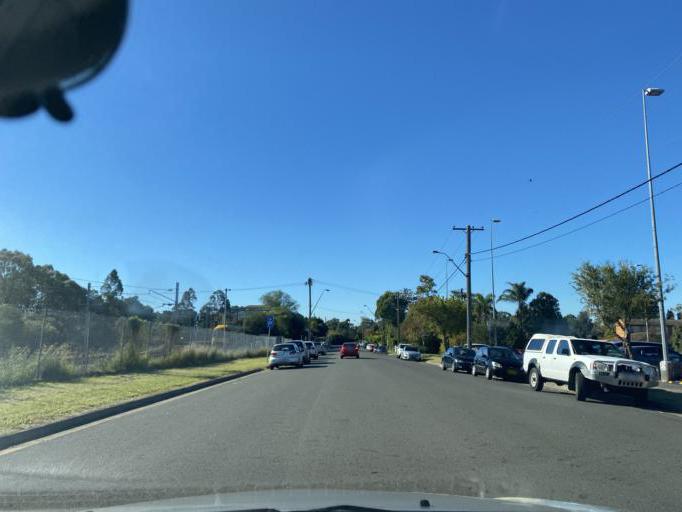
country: AU
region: New South Wales
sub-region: Campbelltown Municipality
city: Ingleburn
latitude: -33.9860
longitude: 150.8778
